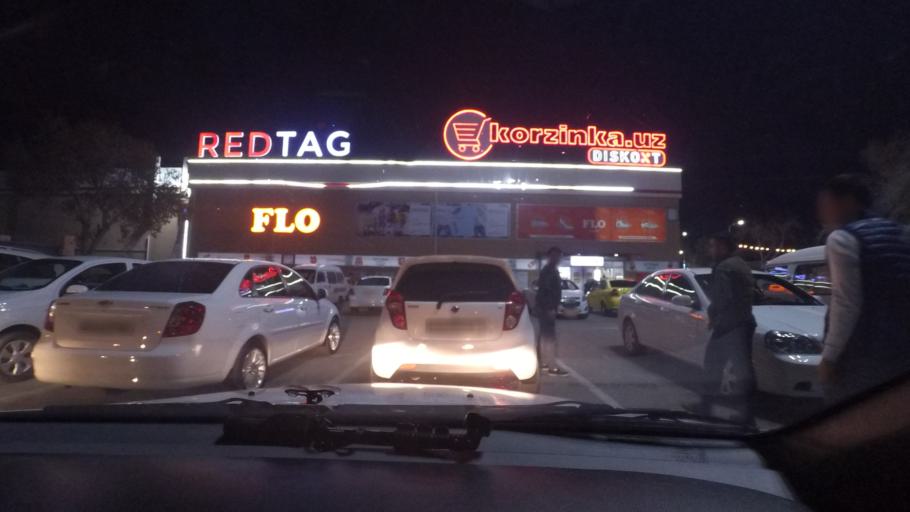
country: UZ
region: Bukhara
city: Bukhara
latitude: 39.7726
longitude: 64.4404
